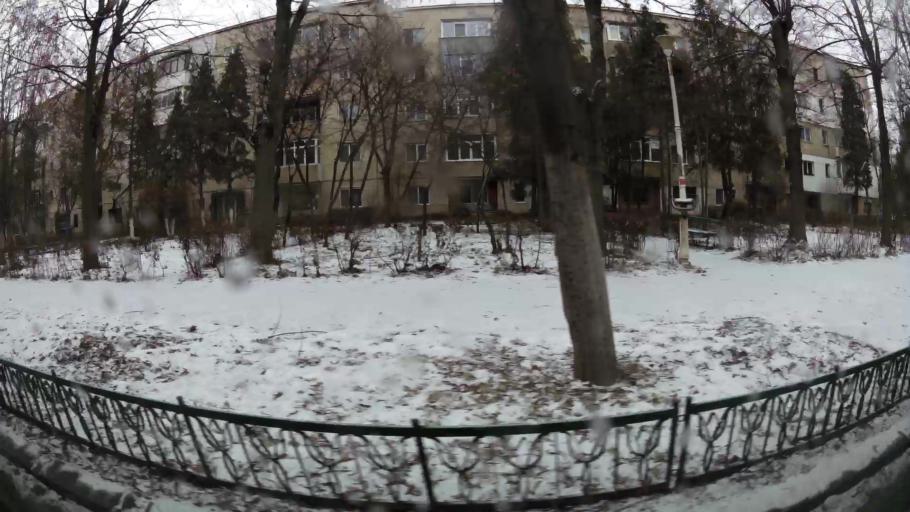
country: RO
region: Prahova
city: Ploiesti
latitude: 44.9552
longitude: 25.9965
